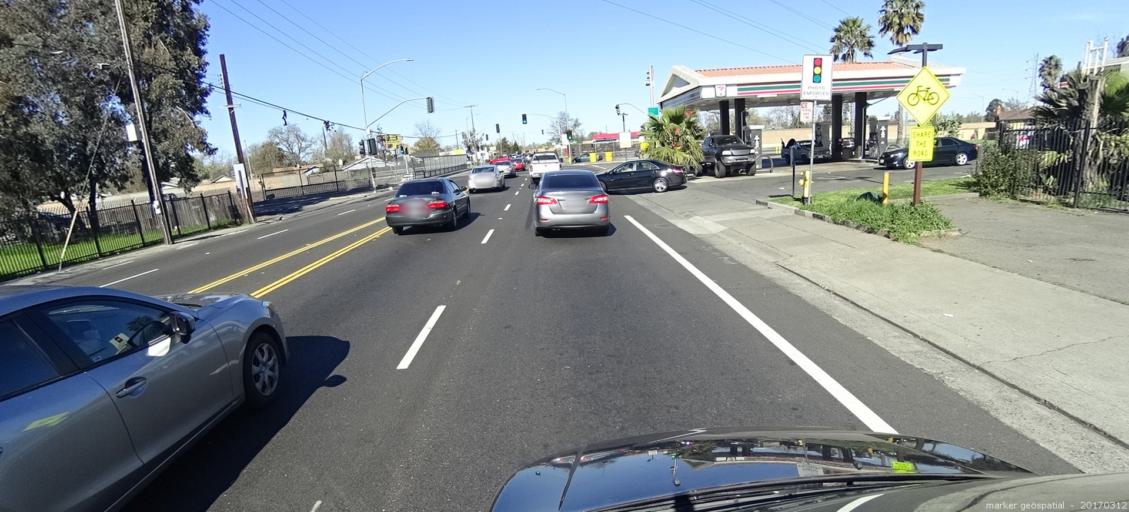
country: US
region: California
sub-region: Sacramento County
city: Arden-Arcade
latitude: 38.6197
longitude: -121.4187
